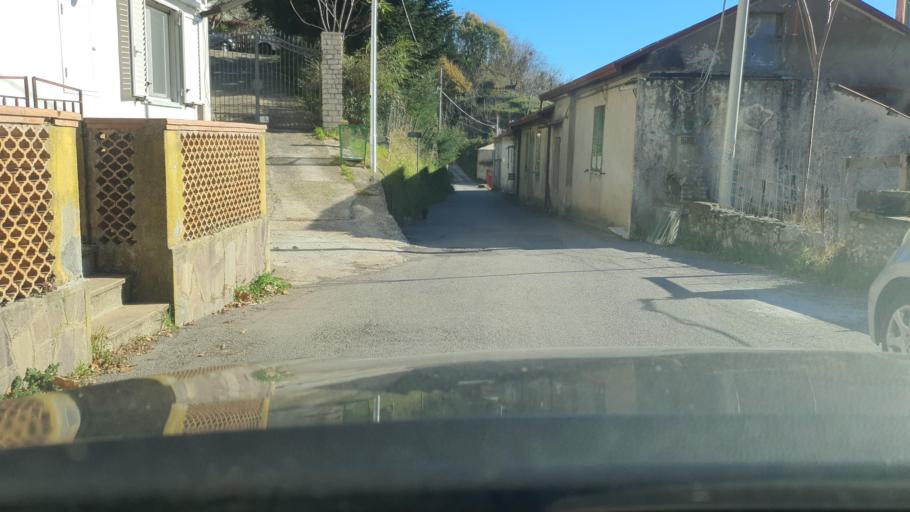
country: IT
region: Calabria
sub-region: Provincia di Catanzaro
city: Sant'Elia
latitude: 38.9583
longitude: 16.5790
